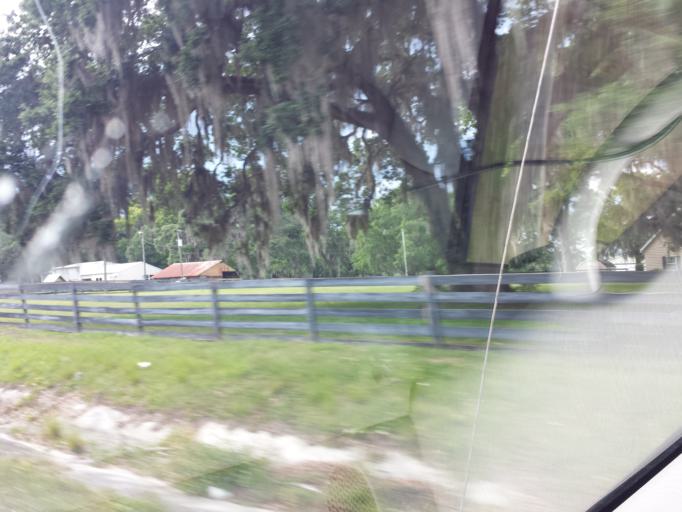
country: US
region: Florida
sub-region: Hernando County
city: Hill 'n Dale
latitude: 28.5532
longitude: -82.3348
